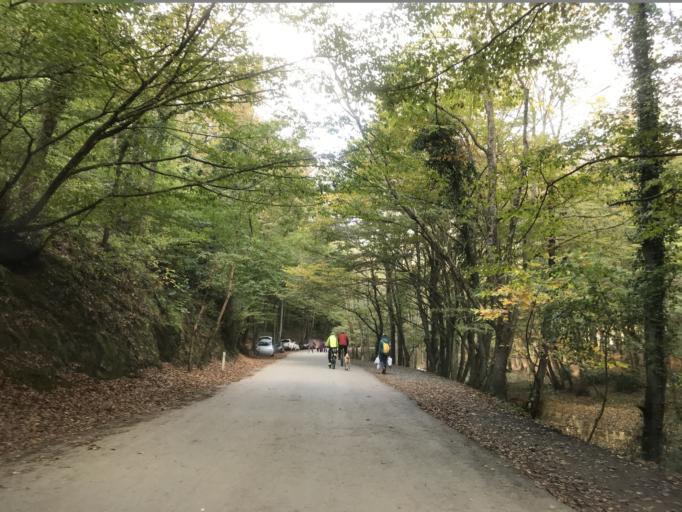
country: TR
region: Istanbul
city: Arikoey
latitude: 41.1872
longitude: 28.9877
